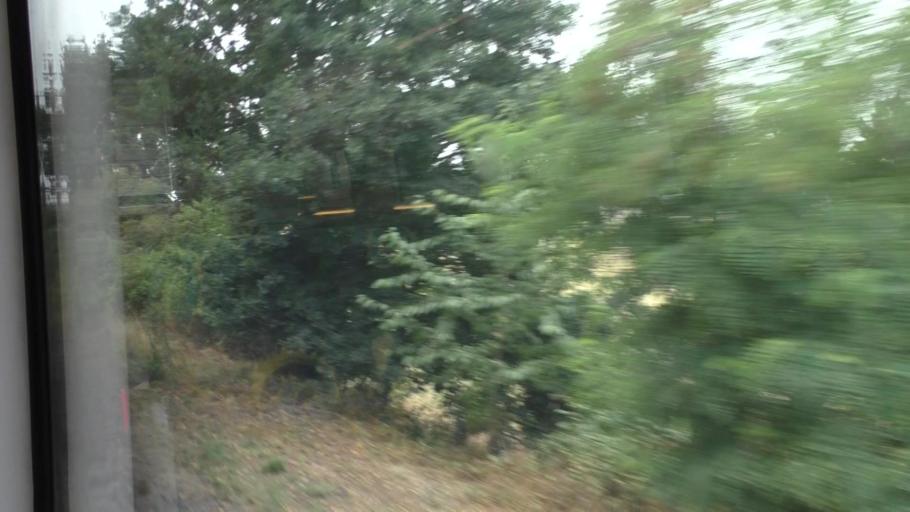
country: DE
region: Saxony
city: Hirschfelde
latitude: 50.9253
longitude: 14.8634
